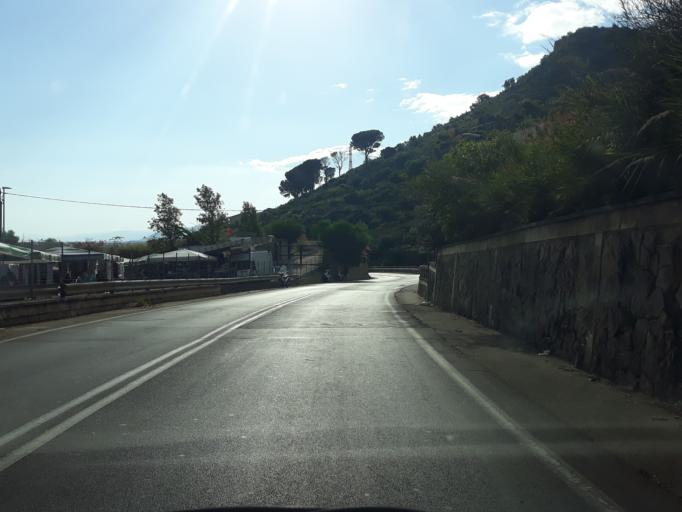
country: IT
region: Sicily
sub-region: Palermo
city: Cefalu
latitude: 38.0331
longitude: 14.0298
